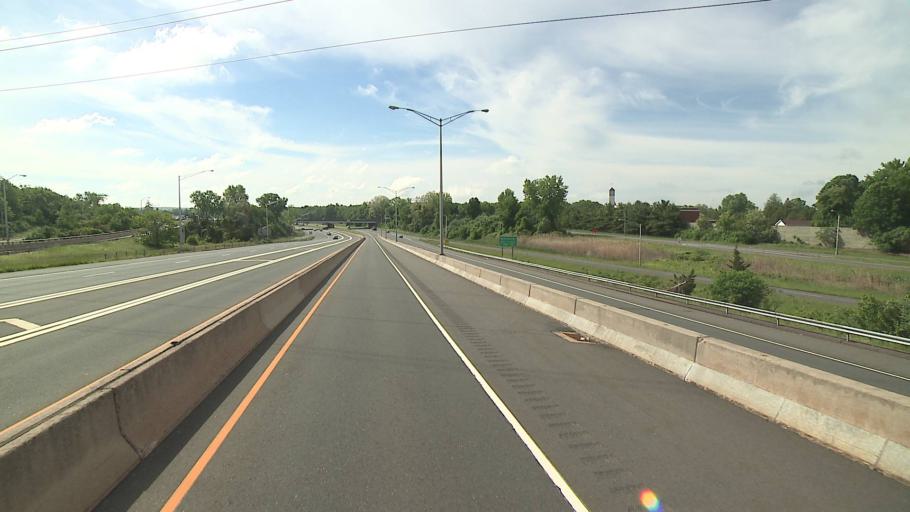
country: US
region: Connecticut
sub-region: Hartford County
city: East Hartford
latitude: 41.7694
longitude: -72.5783
